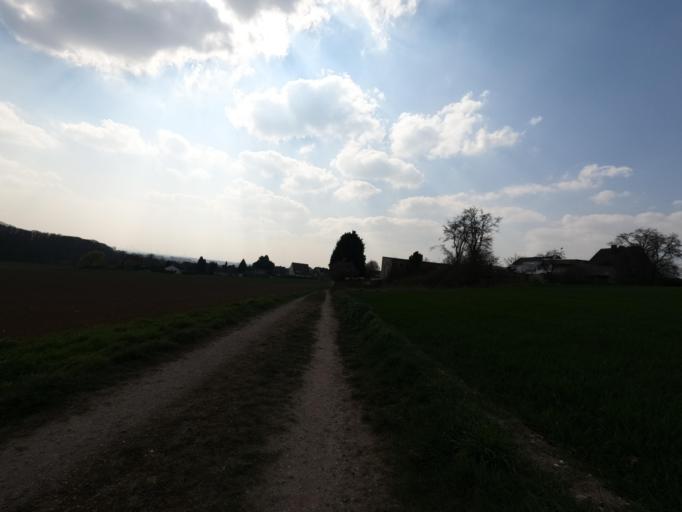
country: DE
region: North Rhine-Westphalia
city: Huckelhoven
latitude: 51.0624
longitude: 6.2327
